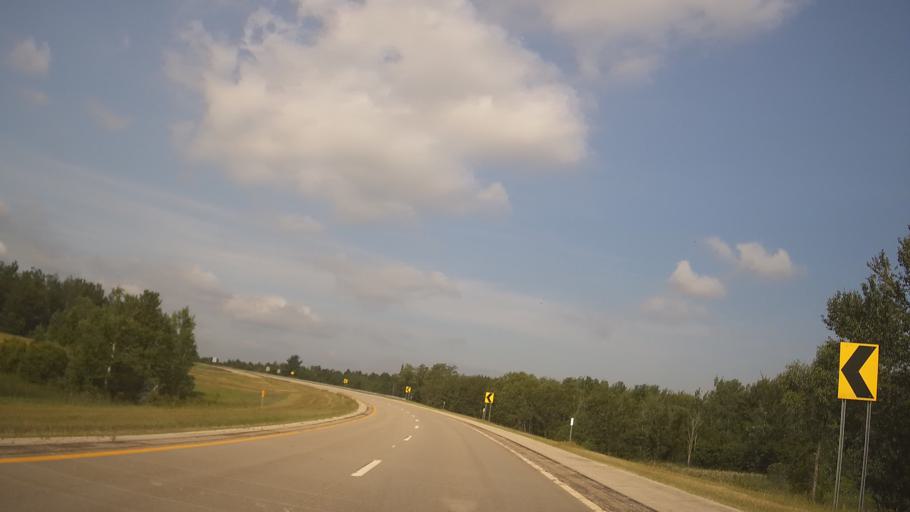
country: US
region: Michigan
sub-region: Roscommon County
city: Saint Helen
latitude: 44.3155
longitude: -84.4971
